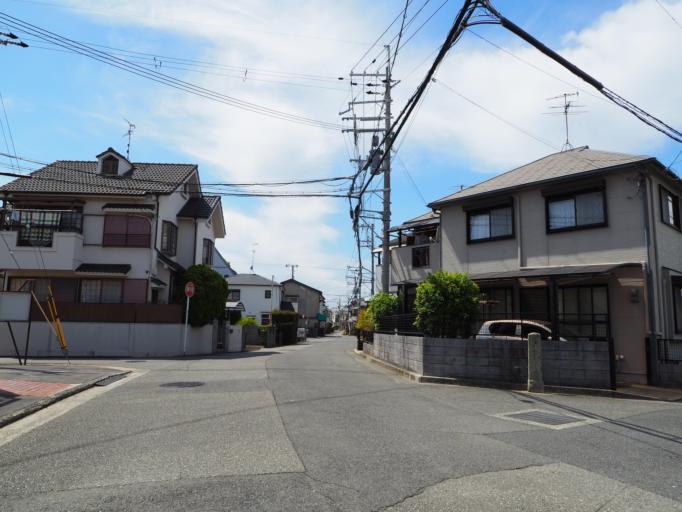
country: JP
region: Hyogo
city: Itami
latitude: 34.7977
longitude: 135.3823
